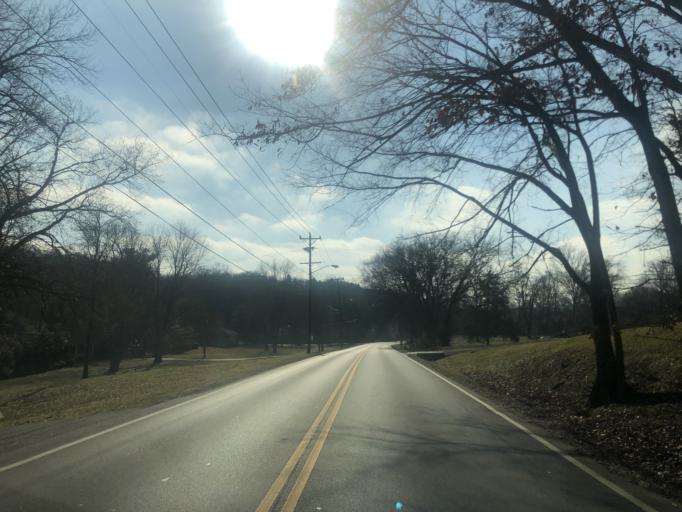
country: US
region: Tennessee
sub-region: Rutherford County
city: La Vergne
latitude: 36.0641
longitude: -86.6631
